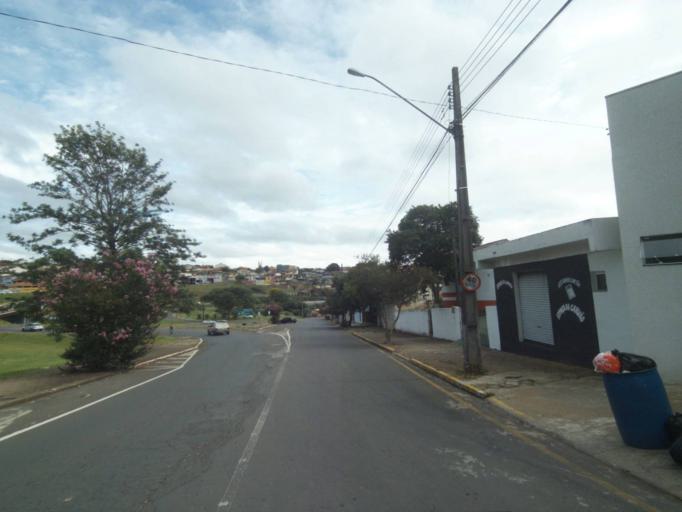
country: BR
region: Parana
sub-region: Telemaco Borba
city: Telemaco Borba
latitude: -24.3266
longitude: -50.6266
